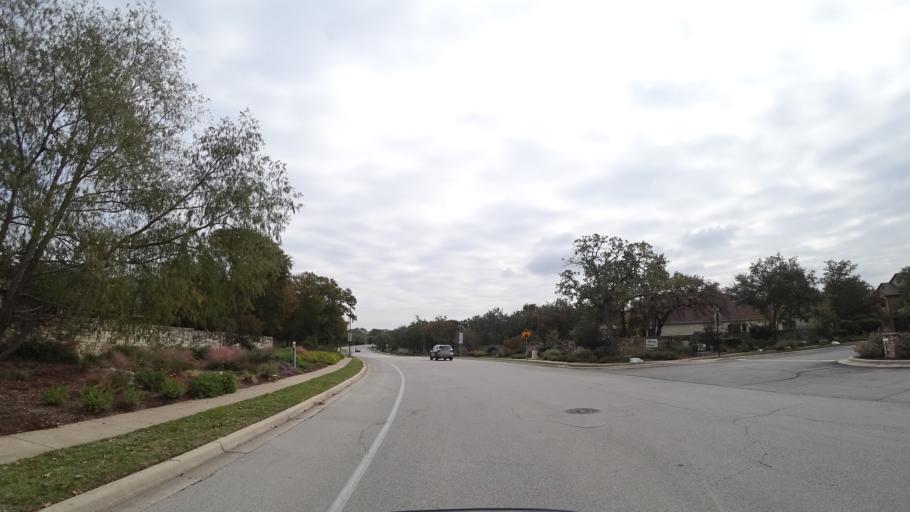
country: US
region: Texas
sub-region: Travis County
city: Shady Hollow
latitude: 30.1932
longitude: -97.9108
